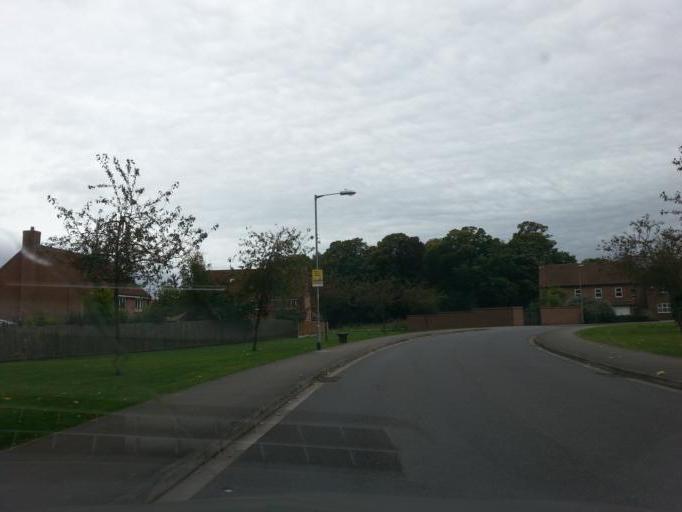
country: GB
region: England
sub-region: Lincolnshire
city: Long Bennington
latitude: 53.0444
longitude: -0.7685
